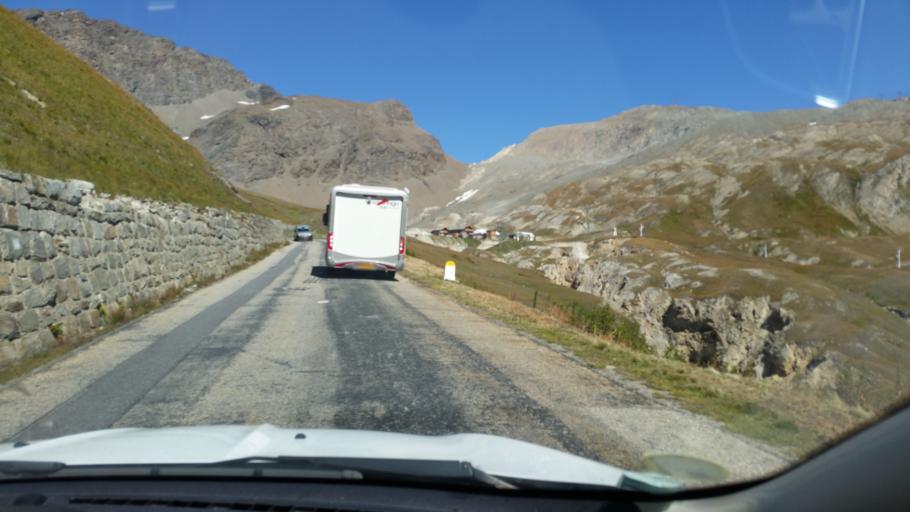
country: FR
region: Rhone-Alpes
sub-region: Departement de la Savoie
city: Val-d'Isere
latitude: 45.4186
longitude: 7.0357
